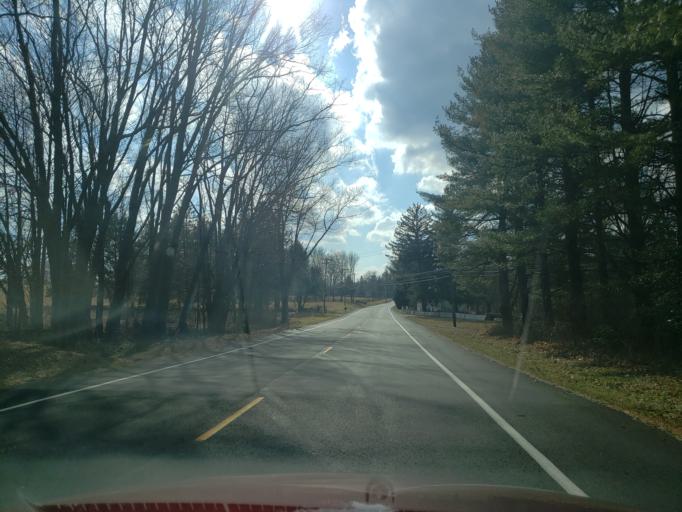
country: US
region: New Jersey
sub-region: Hunterdon County
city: Lambertville
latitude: 40.4391
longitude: -74.9489
